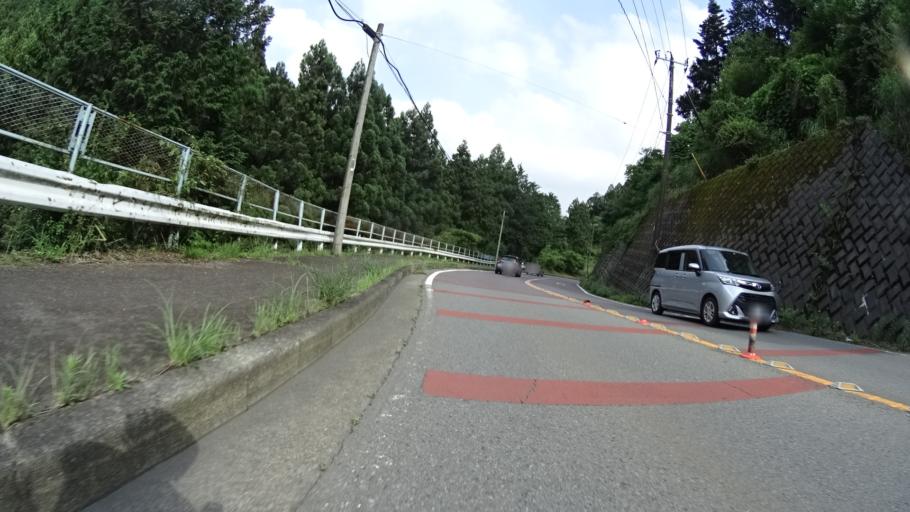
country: JP
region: Kanagawa
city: Atsugi
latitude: 35.5003
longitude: 139.2598
